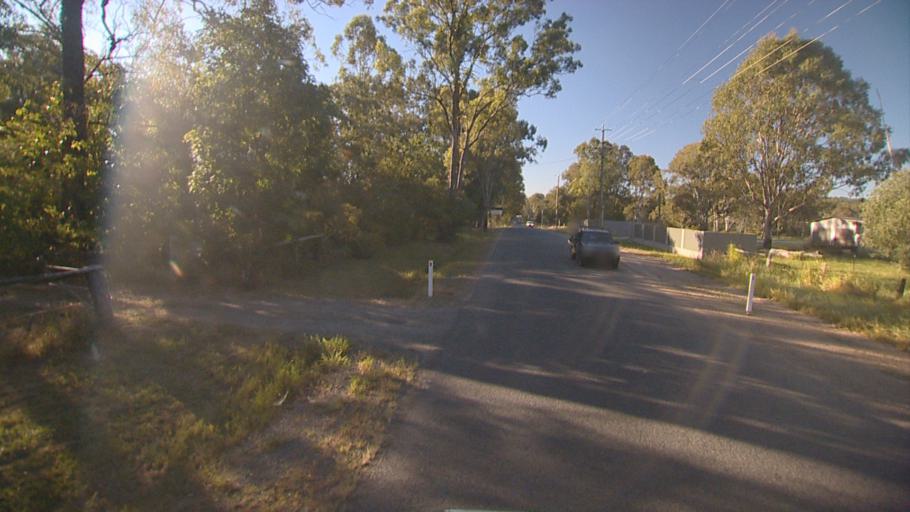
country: AU
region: Queensland
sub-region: Logan
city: Logan Reserve
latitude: -27.7619
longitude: 153.1392
